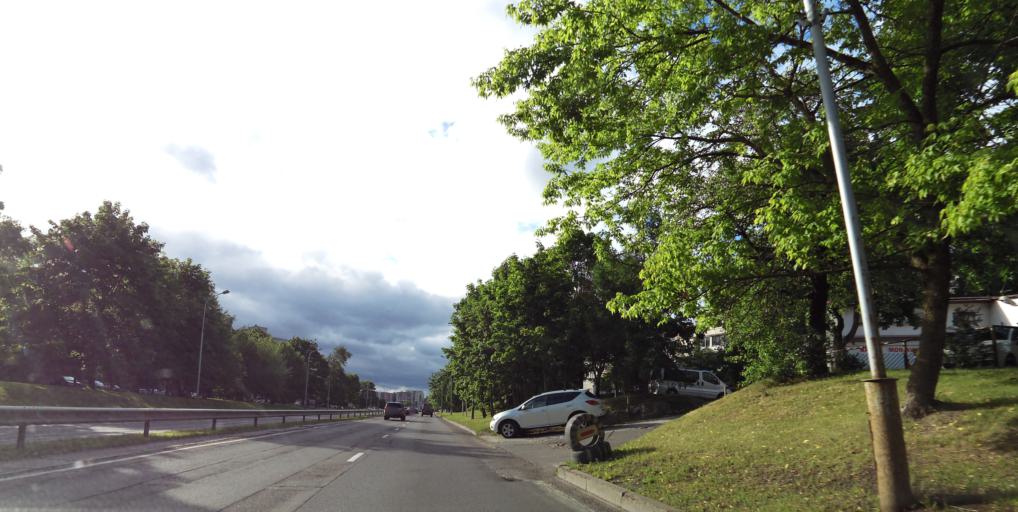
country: LT
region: Vilnius County
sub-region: Vilnius
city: Vilnius
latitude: 54.6993
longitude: 25.2943
